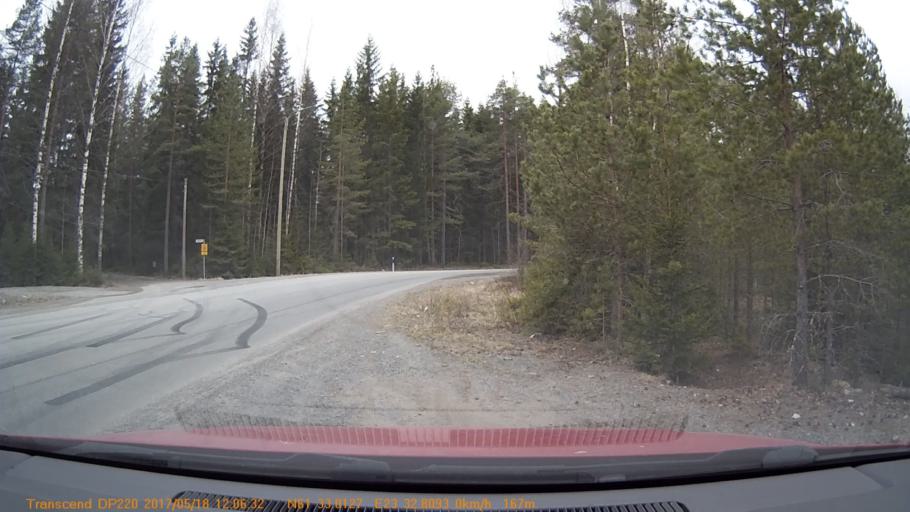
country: FI
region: Pirkanmaa
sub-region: Tampere
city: Yloejaervi
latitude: 61.5503
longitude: 23.5469
